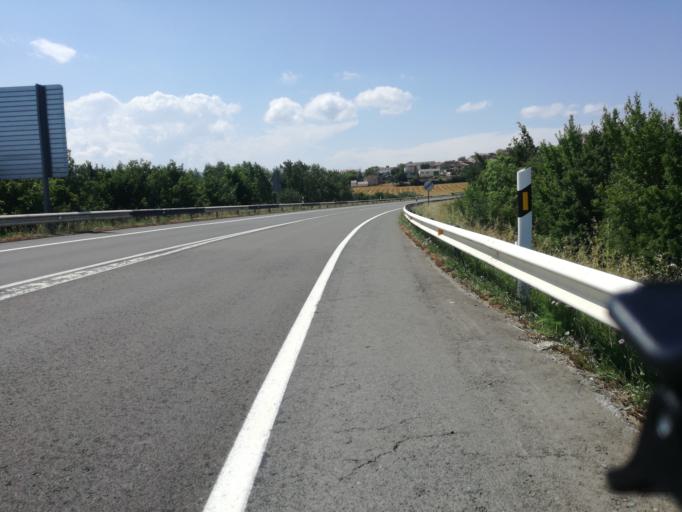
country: ES
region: Basque Country
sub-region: Provincia de Alava
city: Gasteiz / Vitoria
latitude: 42.8623
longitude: -2.7422
